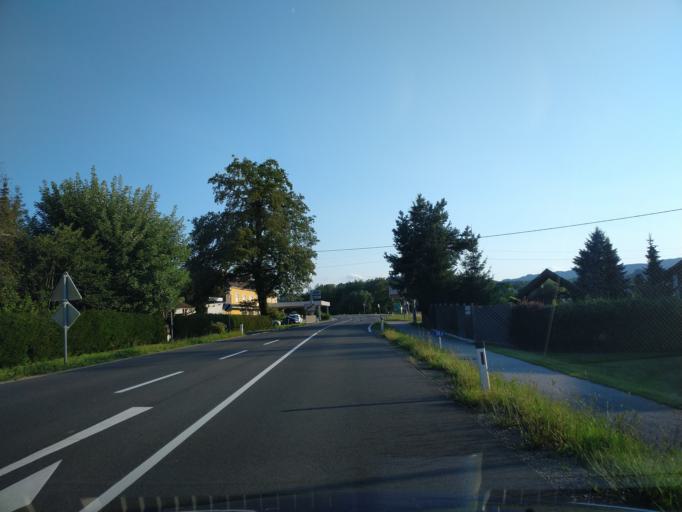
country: AT
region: Styria
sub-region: Politischer Bezirk Deutschlandsberg
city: Wies
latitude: 46.7173
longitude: 15.2541
